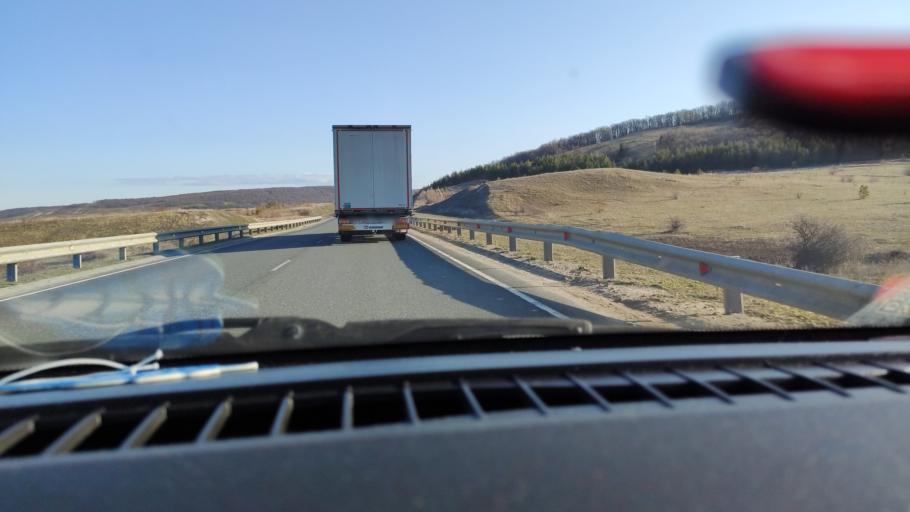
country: RU
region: Saratov
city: Alekseyevka
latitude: 52.3819
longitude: 47.9738
